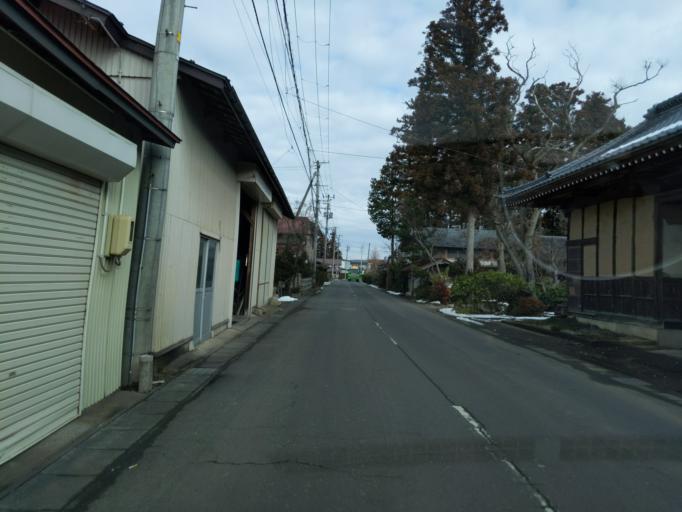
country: JP
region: Iwate
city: Mizusawa
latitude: 39.0856
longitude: 141.1711
